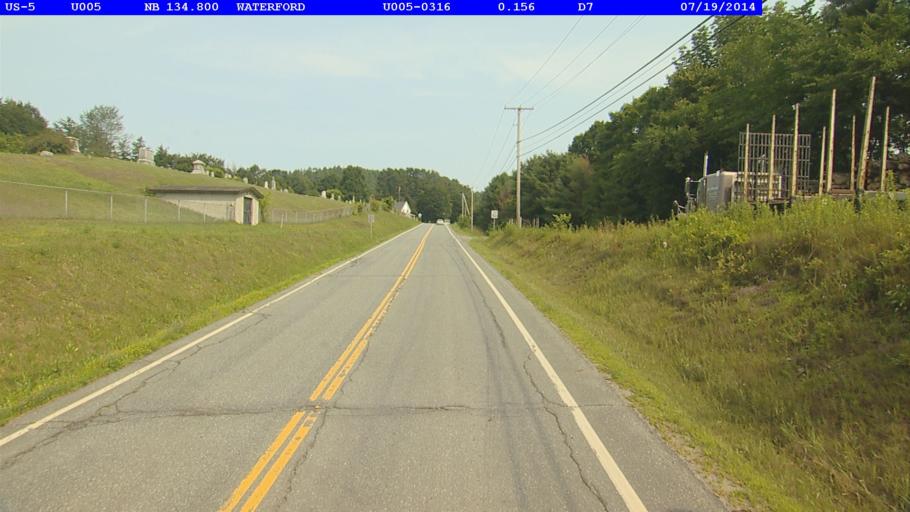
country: US
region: Vermont
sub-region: Caledonia County
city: Saint Johnsbury
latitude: 44.3815
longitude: -72.0263
